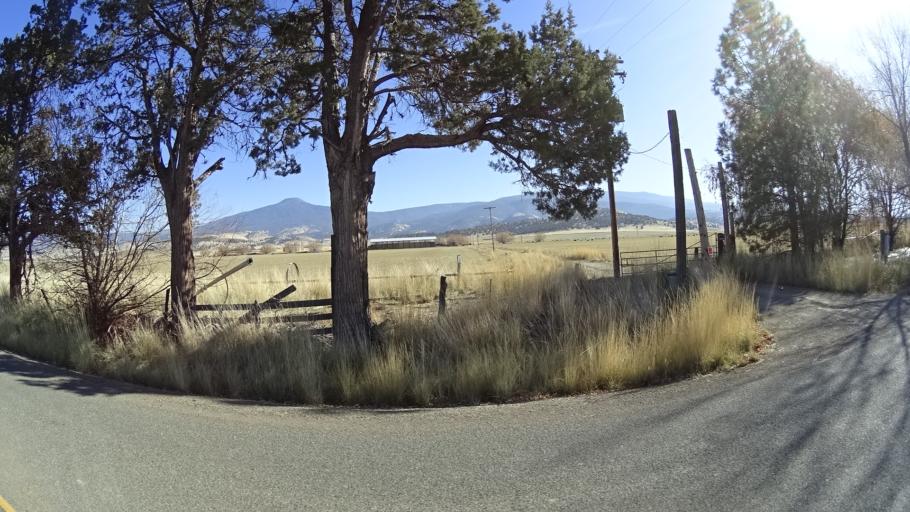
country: US
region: California
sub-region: Siskiyou County
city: Montague
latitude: 41.6796
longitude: -122.3698
